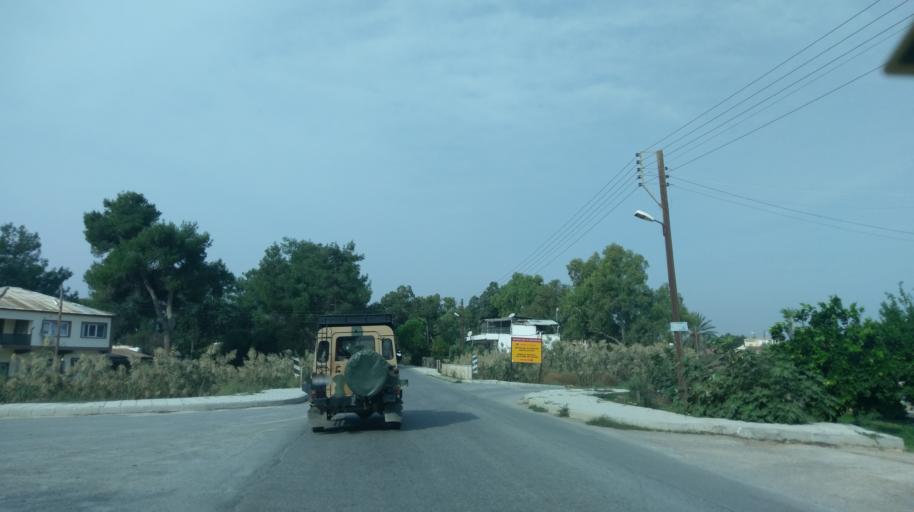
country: CY
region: Lefkosia
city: Mammari
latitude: 35.2306
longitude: 33.1681
